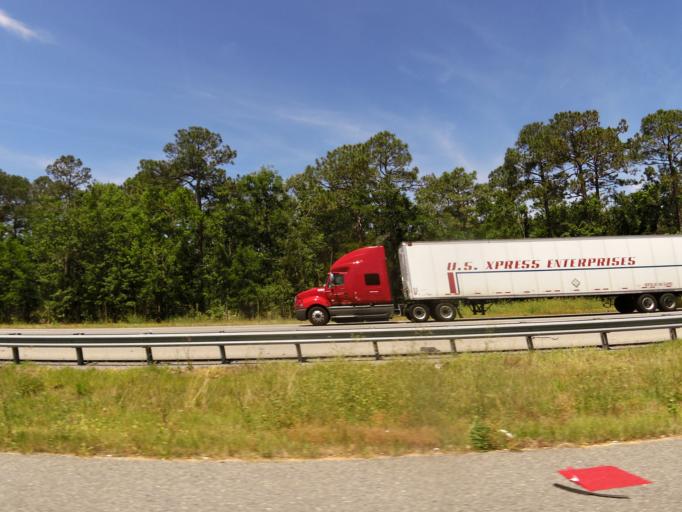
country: US
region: Georgia
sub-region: Glynn County
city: Dock Junction
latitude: 31.1762
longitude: -81.5476
